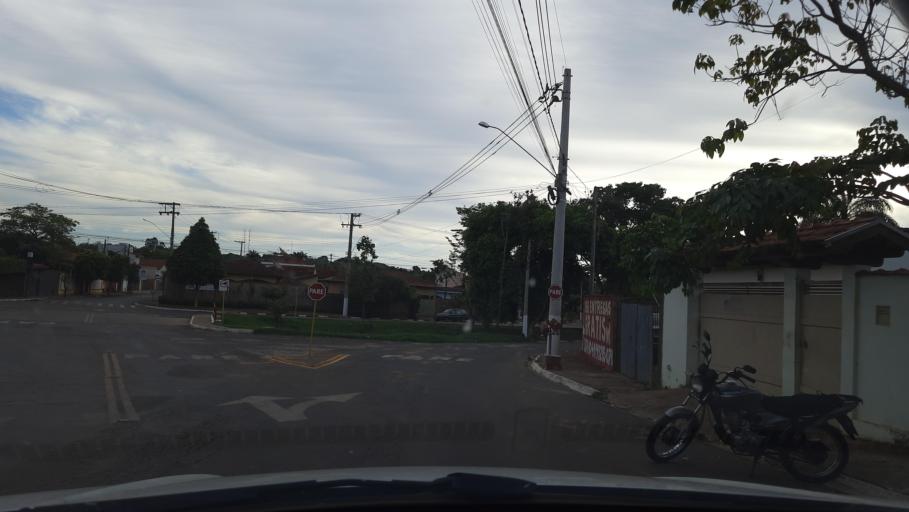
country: BR
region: Sao Paulo
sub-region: Casa Branca
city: Casa Branca
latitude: -21.7668
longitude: -47.0887
